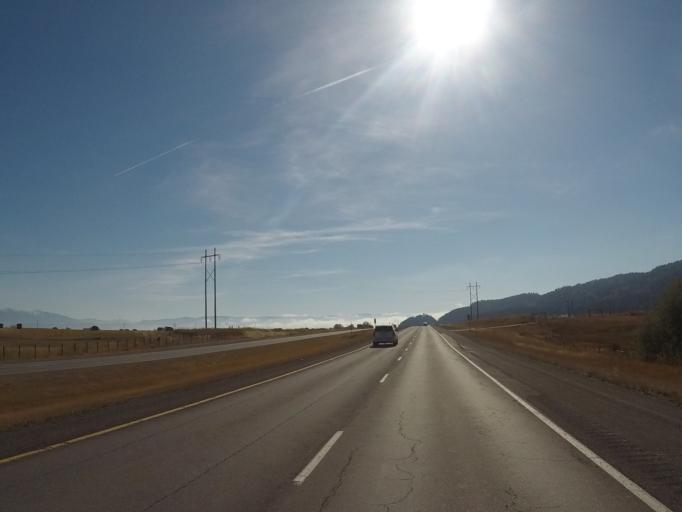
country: US
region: Montana
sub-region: Flathead County
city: Somers
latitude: 48.1133
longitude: -114.2523
